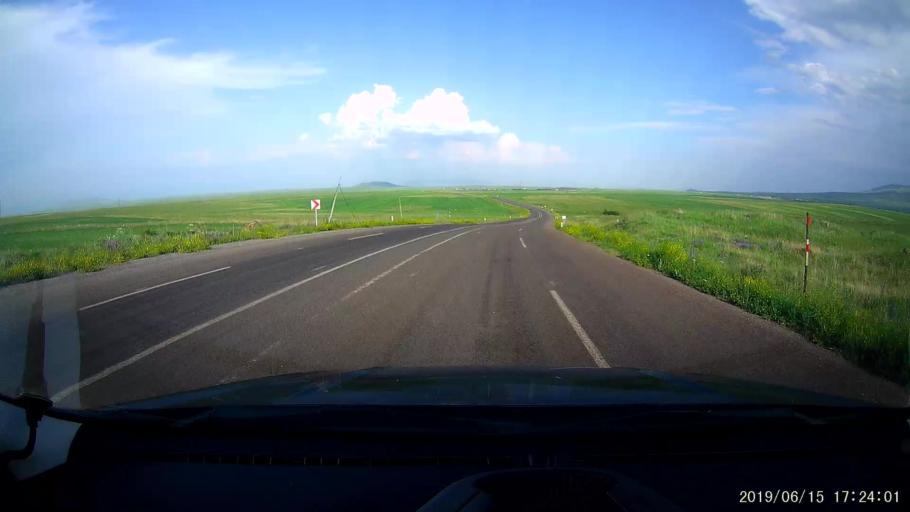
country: TR
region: Kars
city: Basgedikler
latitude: 40.6161
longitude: 43.3749
